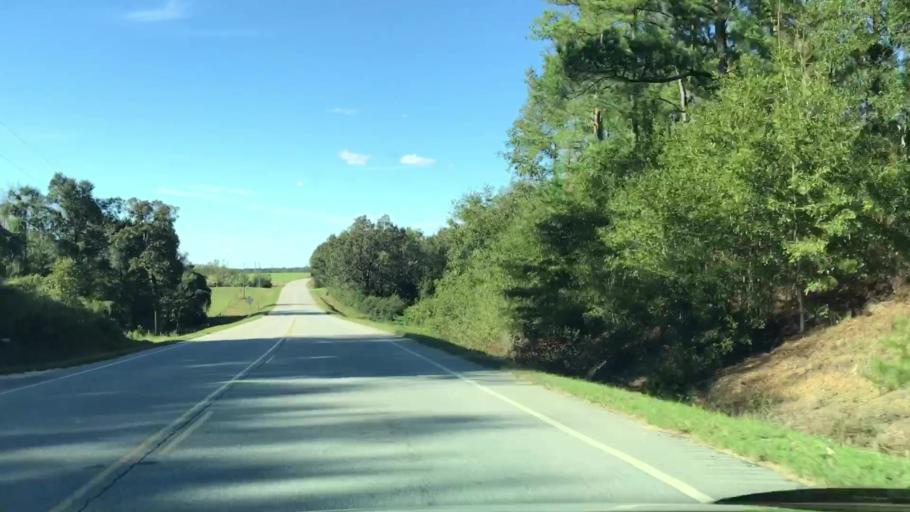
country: US
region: Georgia
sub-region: Jefferson County
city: Louisville
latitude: 33.0713
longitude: -82.4079
